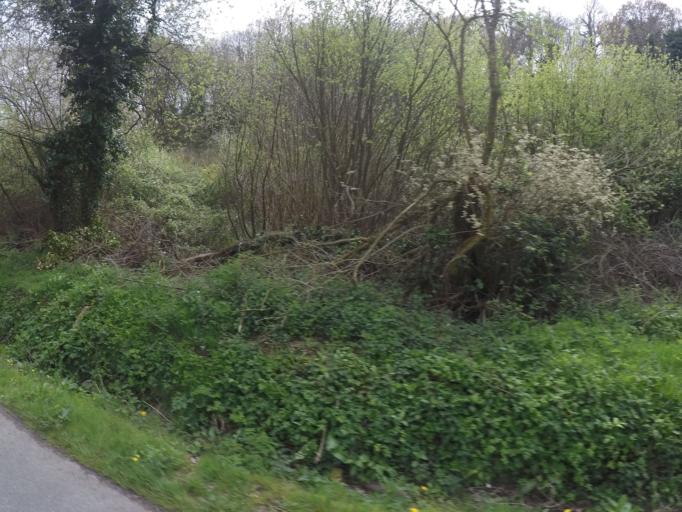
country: FR
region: Brittany
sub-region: Departement des Cotes-d'Armor
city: Plouezec
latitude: 48.7314
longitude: -2.9521
